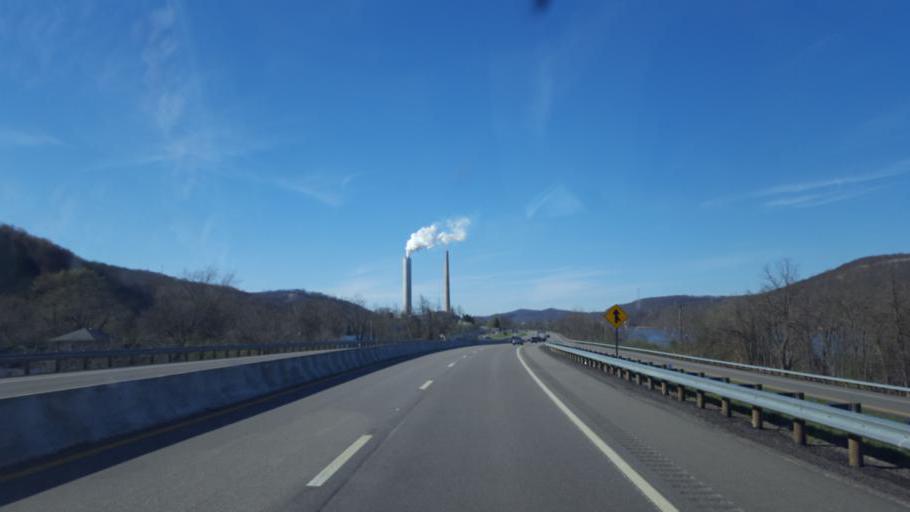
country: US
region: West Virginia
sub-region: Hancock County
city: New Cumberland
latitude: 40.5085
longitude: -80.6220
